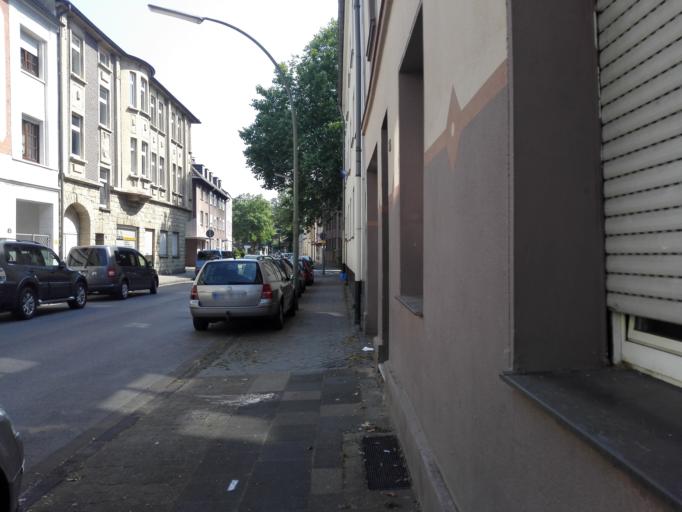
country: DE
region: North Rhine-Westphalia
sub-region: Regierungsbezirk Munster
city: Gladbeck
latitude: 51.5304
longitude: 7.0248
